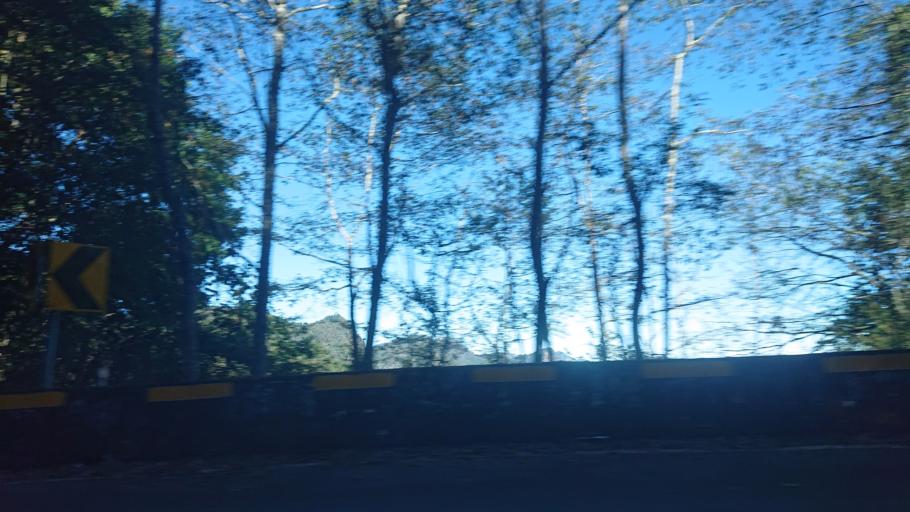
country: TW
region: Taiwan
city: Lugu
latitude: 23.4781
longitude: 120.8366
